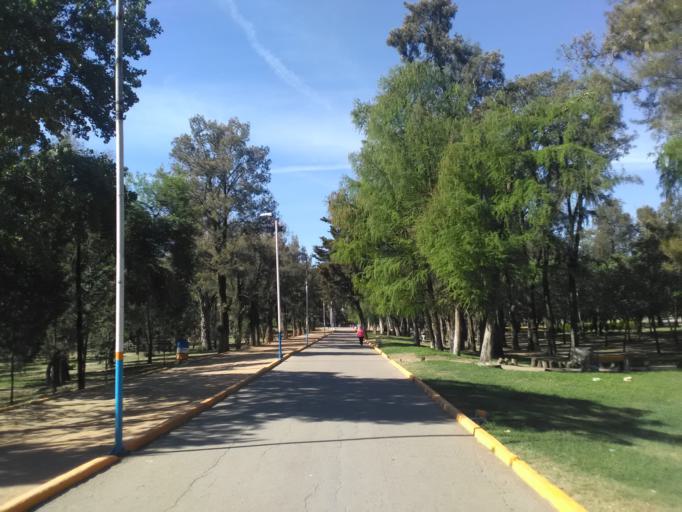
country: MX
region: Durango
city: Victoria de Durango
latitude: 24.0271
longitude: -104.6860
